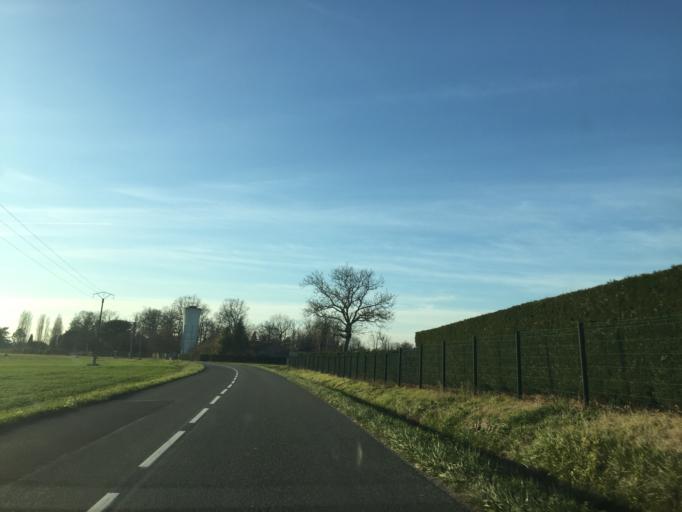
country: FR
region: Poitou-Charentes
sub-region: Departement de la Charente
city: Chalais
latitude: 45.2709
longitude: 0.0649
